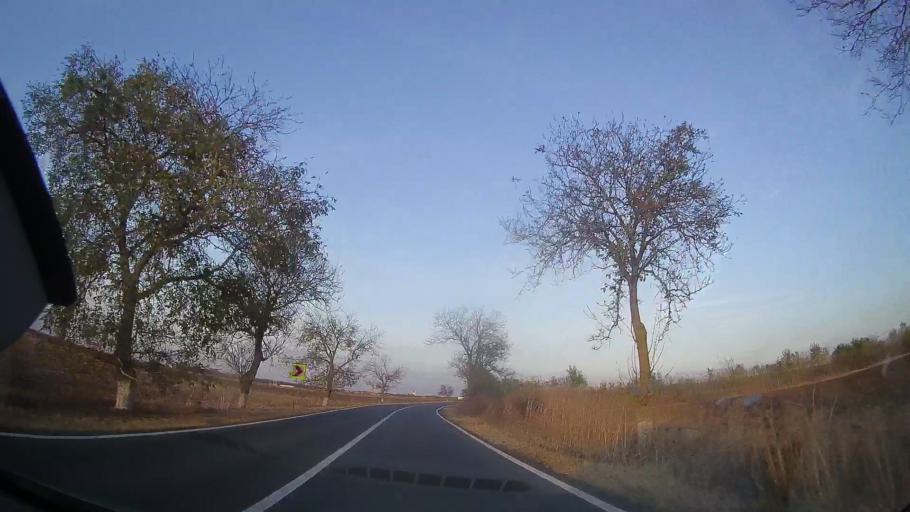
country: RO
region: Constanta
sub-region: Comuna Topraisar
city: Topraisar
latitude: 43.9992
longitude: 28.4329
